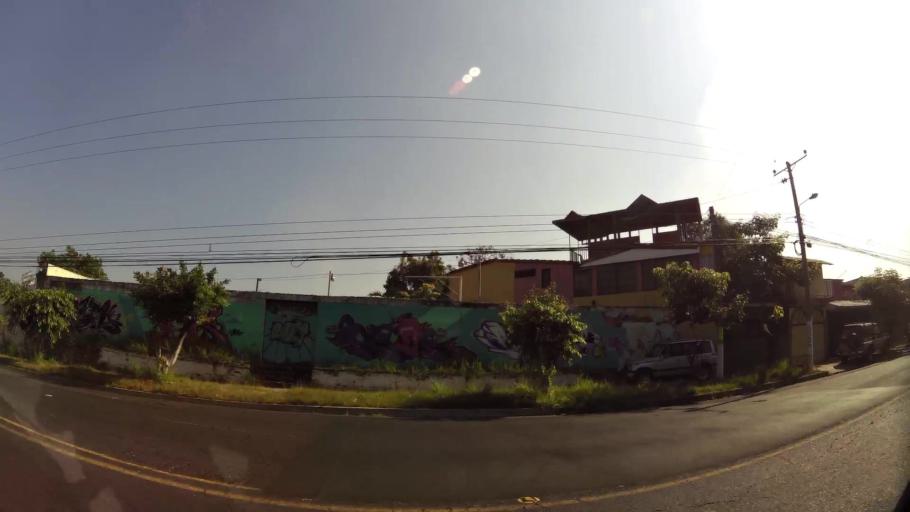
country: SV
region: La Libertad
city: Antiguo Cuscatlan
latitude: 13.6700
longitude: -89.2281
